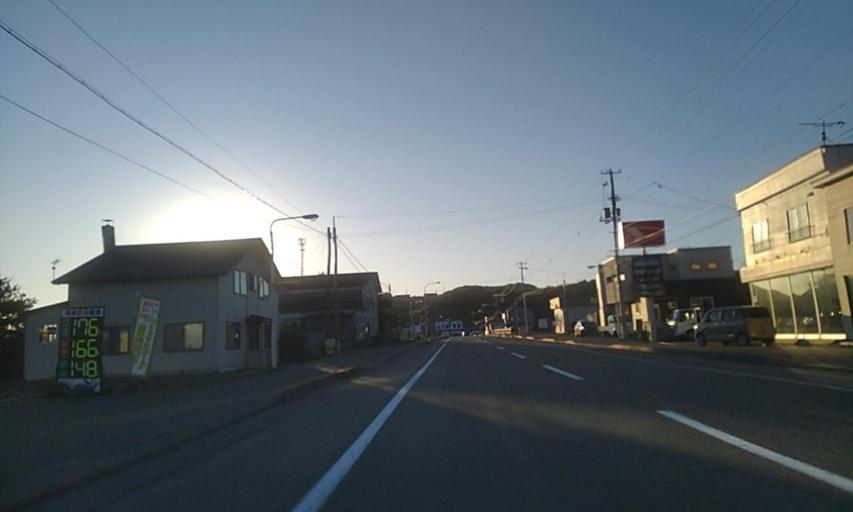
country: JP
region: Hokkaido
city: Shizunai-furukawacho
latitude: 42.1275
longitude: 142.9311
